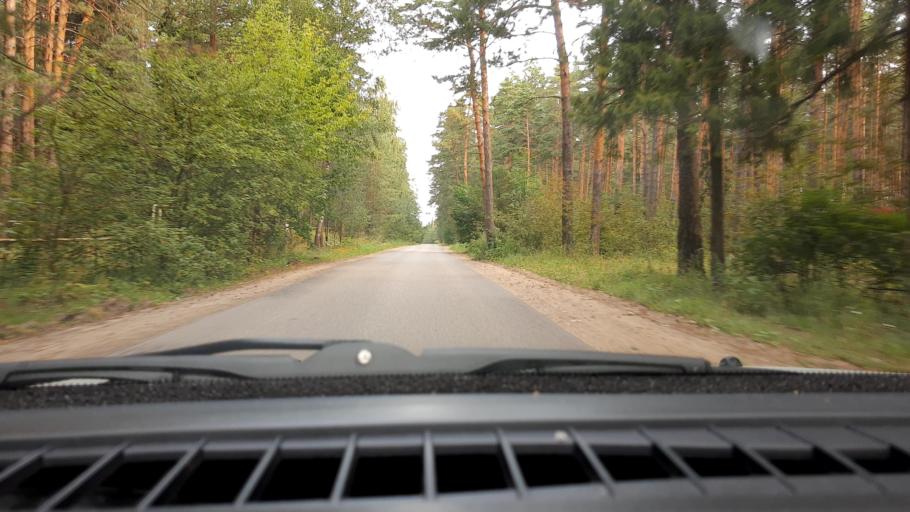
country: RU
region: Nizjnij Novgorod
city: Afonino
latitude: 56.1825
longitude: 44.0799
